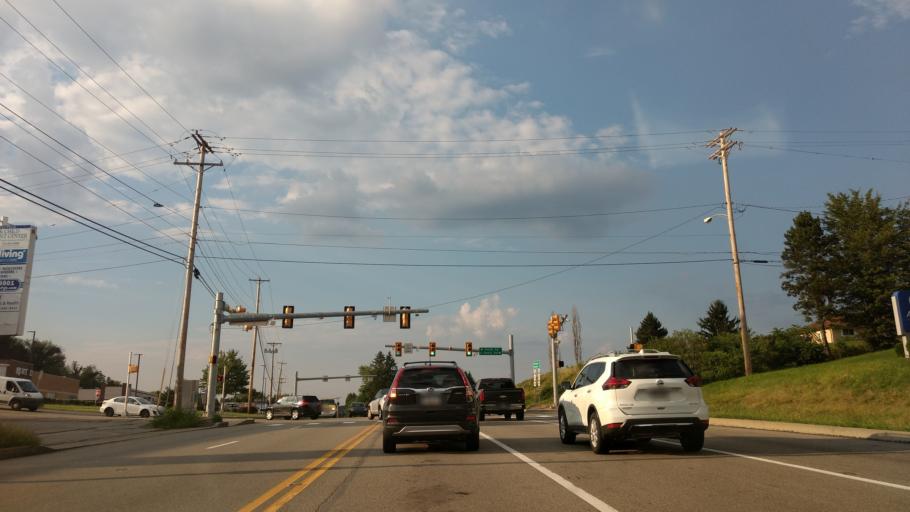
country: US
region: Pennsylvania
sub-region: Allegheny County
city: Bakerstown
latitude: 40.6251
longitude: -79.9419
